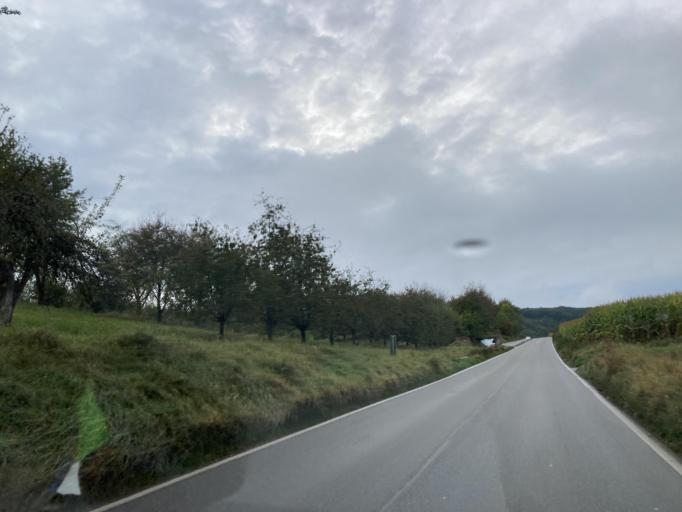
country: DE
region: Baden-Wuerttemberg
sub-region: Freiburg Region
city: Feldberg
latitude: 47.7747
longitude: 7.6249
